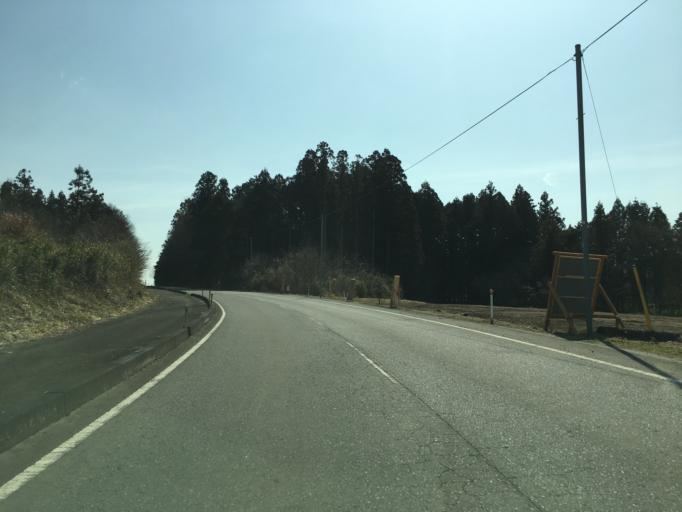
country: JP
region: Fukushima
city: Ishikawa
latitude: 37.1297
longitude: 140.4102
